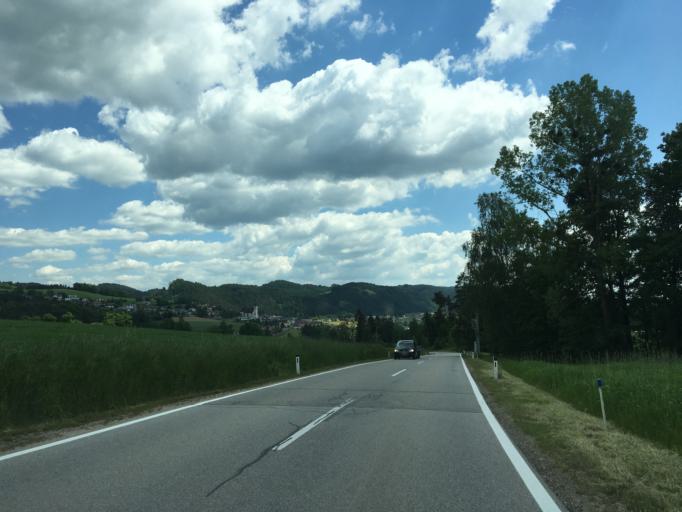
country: AT
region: Upper Austria
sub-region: Politischer Bezirk Freistadt
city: Freistadt
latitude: 48.4492
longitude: 14.5237
